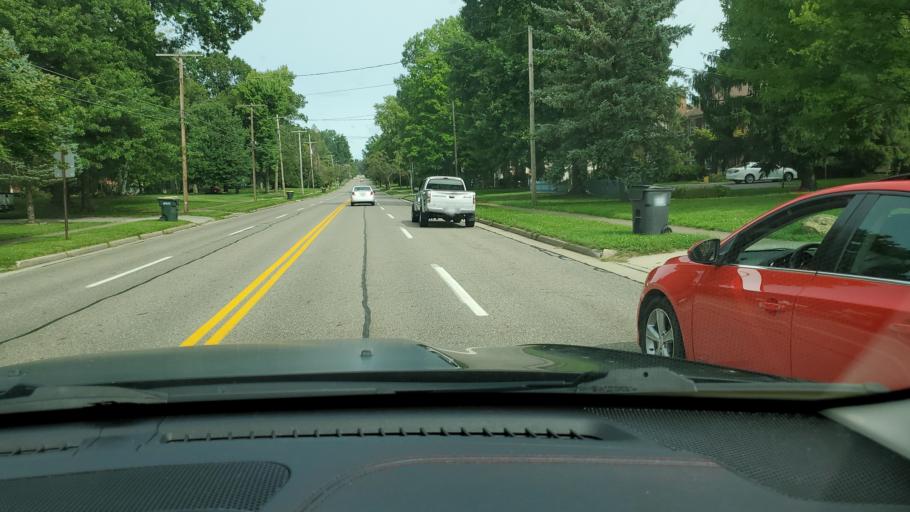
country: US
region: Ohio
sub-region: Mahoning County
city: Boardman
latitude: 41.0361
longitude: -80.6723
